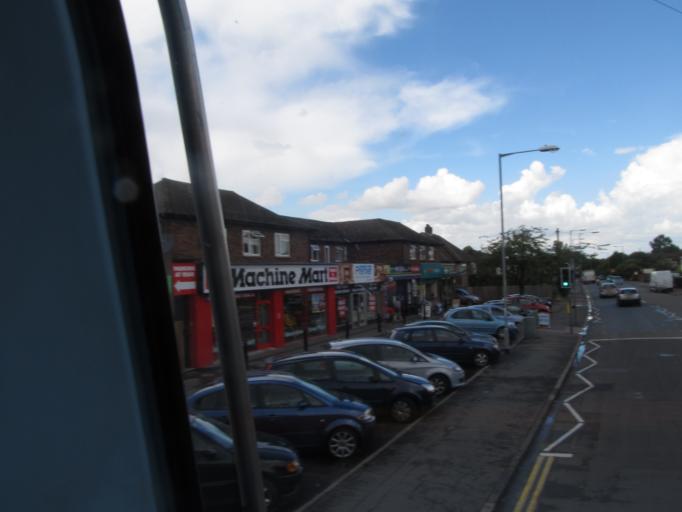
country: GB
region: England
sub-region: Cambridgeshire
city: Cambridge
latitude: 52.2200
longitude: 0.1117
